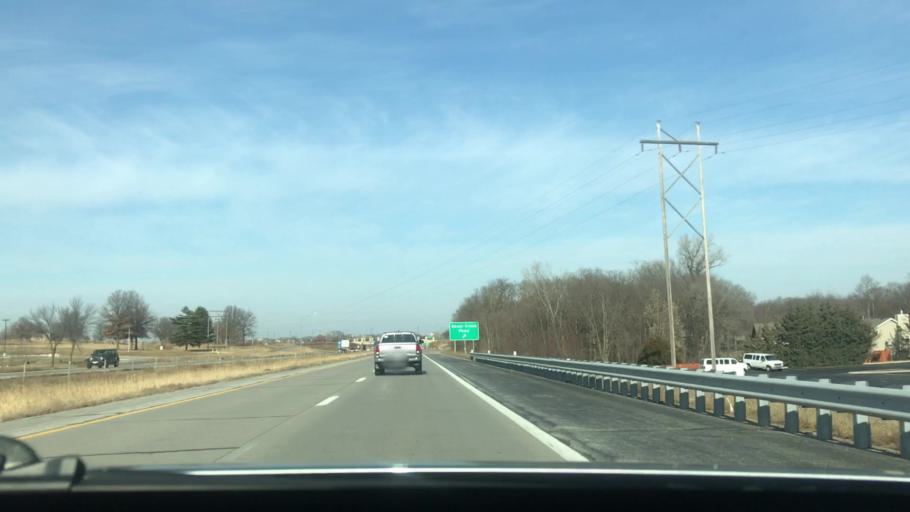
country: US
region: Missouri
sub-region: Clay County
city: Gladstone
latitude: 39.2829
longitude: -94.5849
